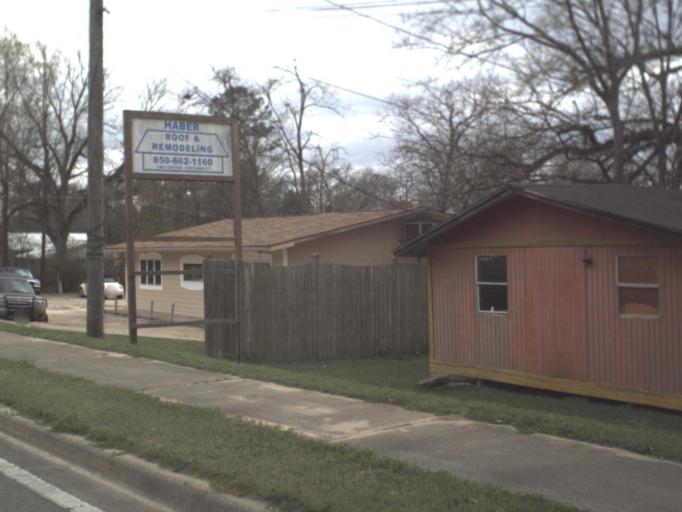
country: US
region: Florida
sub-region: Gadsden County
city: Quincy
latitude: 30.5618
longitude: -84.5925
